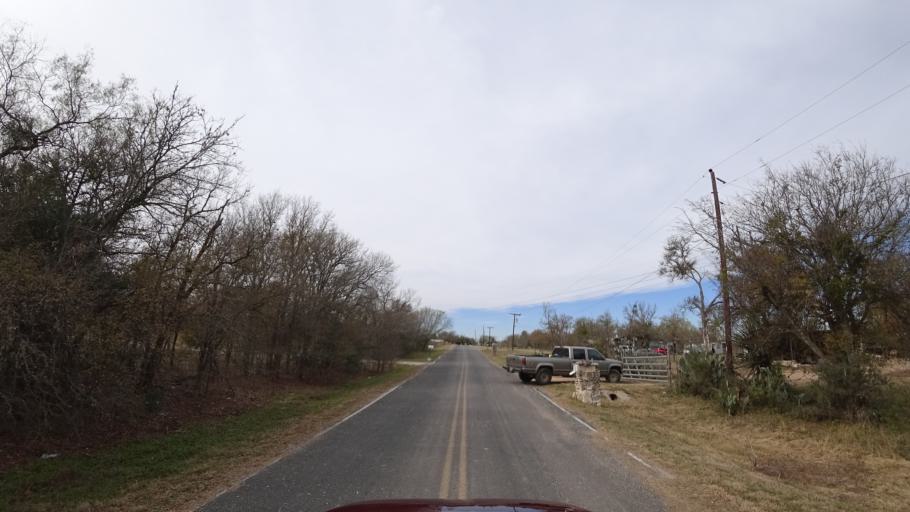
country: US
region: Texas
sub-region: Travis County
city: Garfield
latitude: 30.1402
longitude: -97.5735
